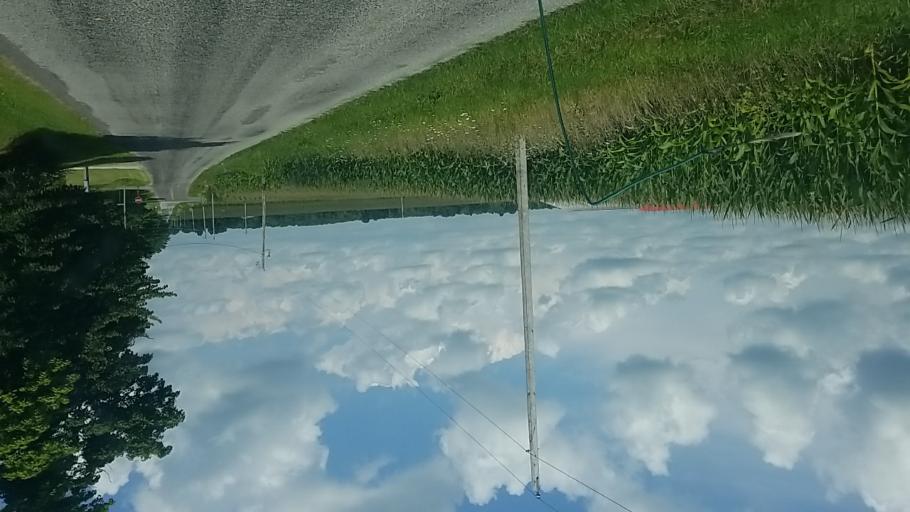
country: US
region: Ohio
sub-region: Wayne County
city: West Salem
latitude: 40.9998
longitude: -82.0783
